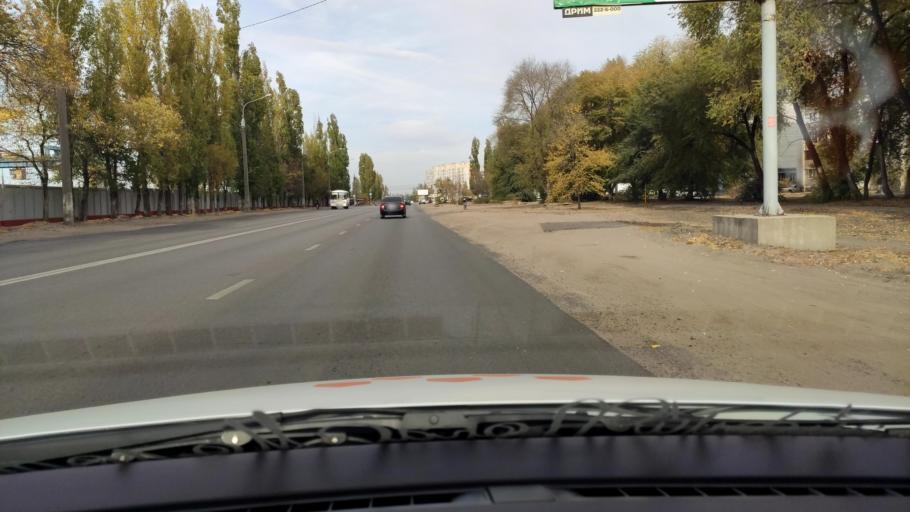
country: RU
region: Voronezj
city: Voronezh
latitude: 51.6393
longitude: 39.2649
